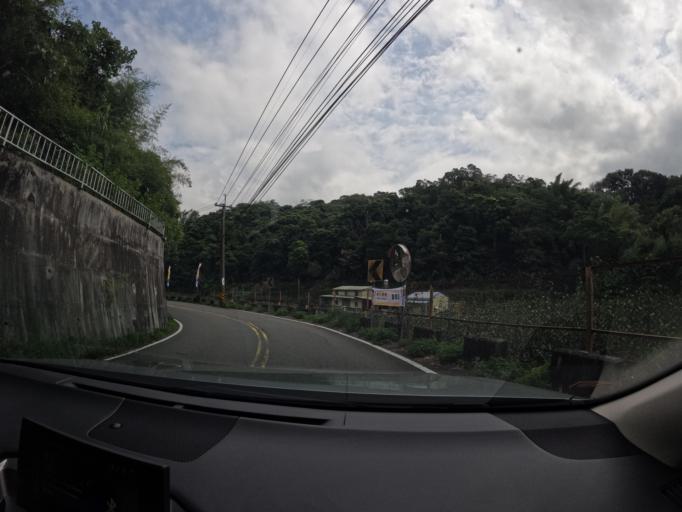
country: TW
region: Taiwan
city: Fengyuan
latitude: 24.3041
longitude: 120.8435
